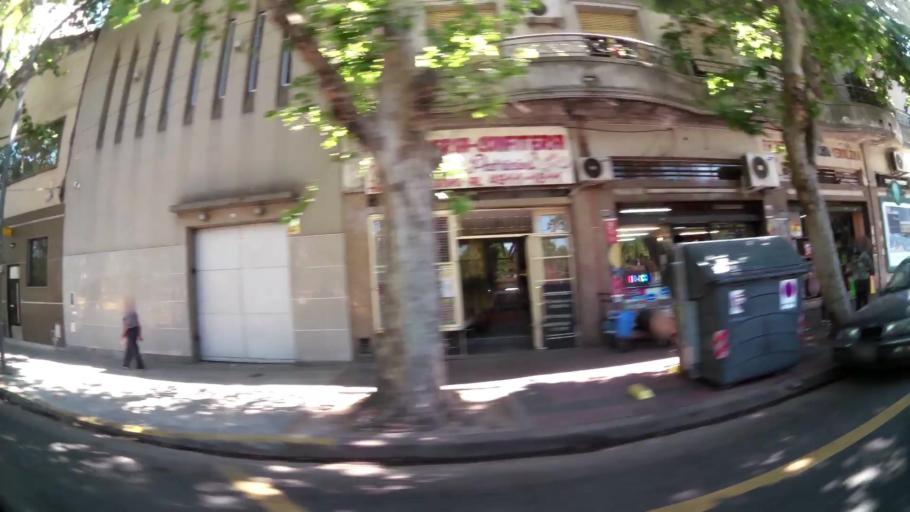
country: AR
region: Buenos Aires F.D.
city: Buenos Aires
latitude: -34.6377
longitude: -58.4093
